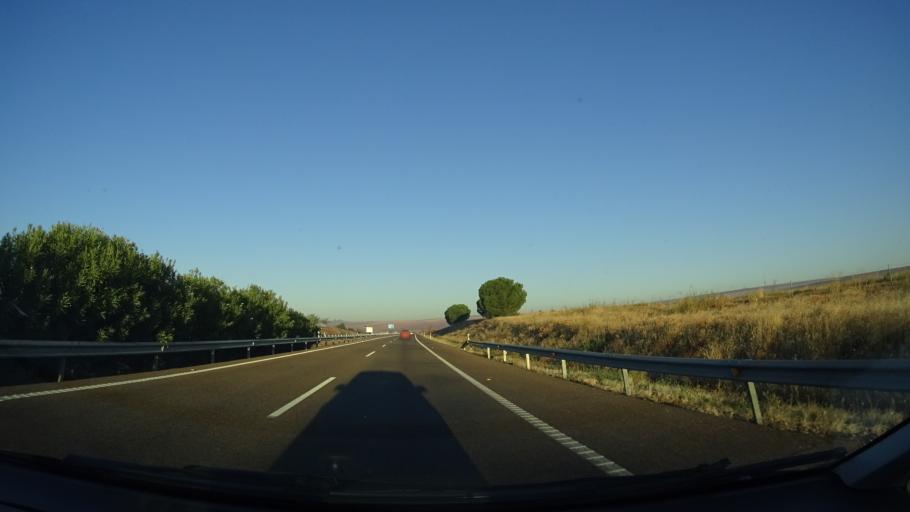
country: ES
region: Extremadura
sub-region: Provincia de Badajoz
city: Merida
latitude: 38.9457
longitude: -6.3125
